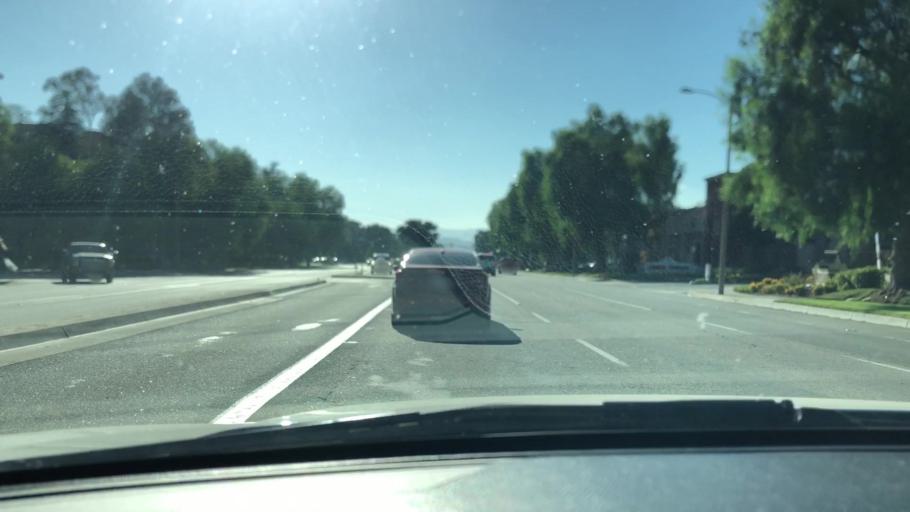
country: US
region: California
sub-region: Los Angeles County
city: Santa Clarita
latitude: 34.4191
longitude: -118.5601
